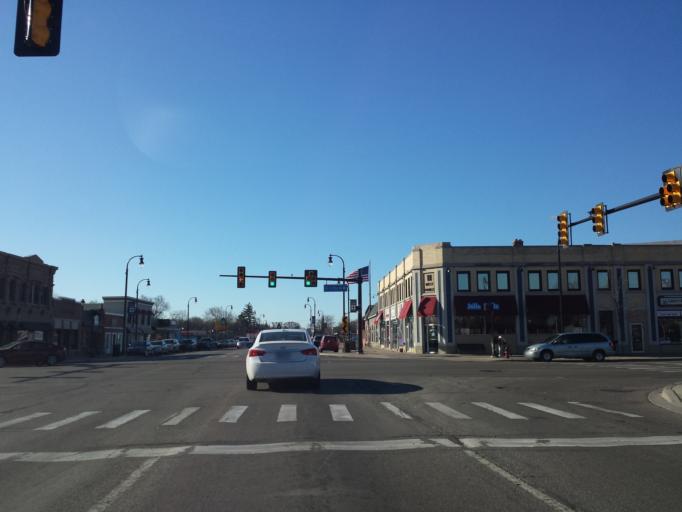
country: US
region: Michigan
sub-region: Oakland County
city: Clawson
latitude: 42.5337
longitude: -83.1464
